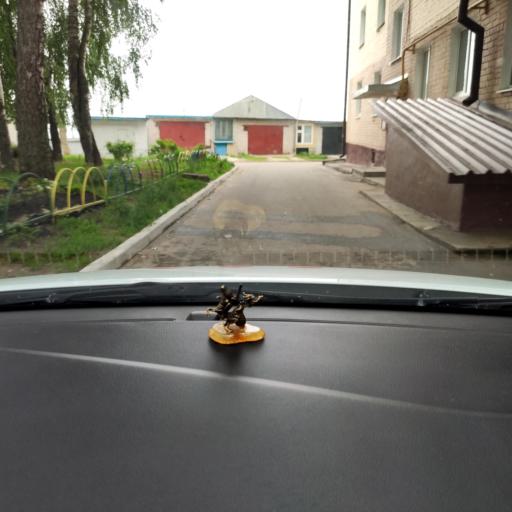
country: RU
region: Tatarstan
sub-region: Zelenodol'skiy Rayon
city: Zelenodolsk
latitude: 55.8464
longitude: 48.5582
